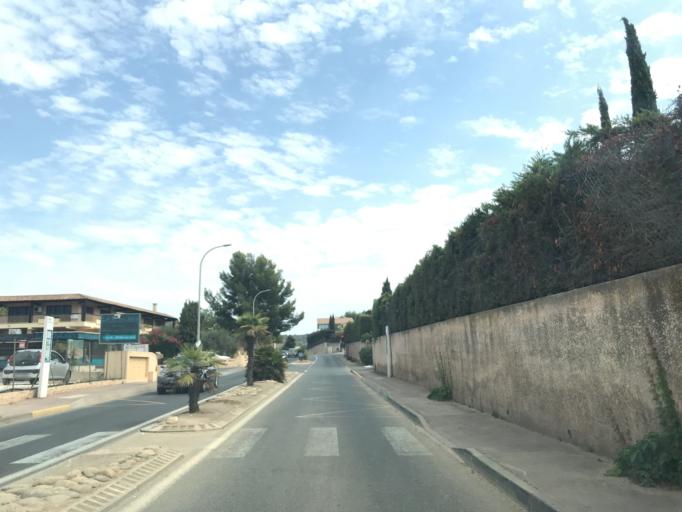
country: FR
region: Provence-Alpes-Cote d'Azur
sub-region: Departement du Var
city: Six-Fours-les-Plages
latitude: 43.0892
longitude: 5.8292
